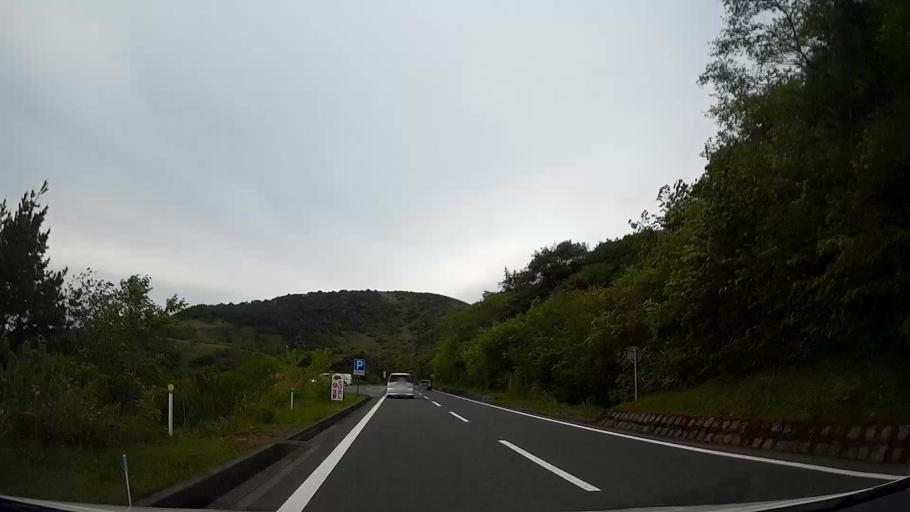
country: JP
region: Shizuoka
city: Atami
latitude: 35.0777
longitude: 139.0267
